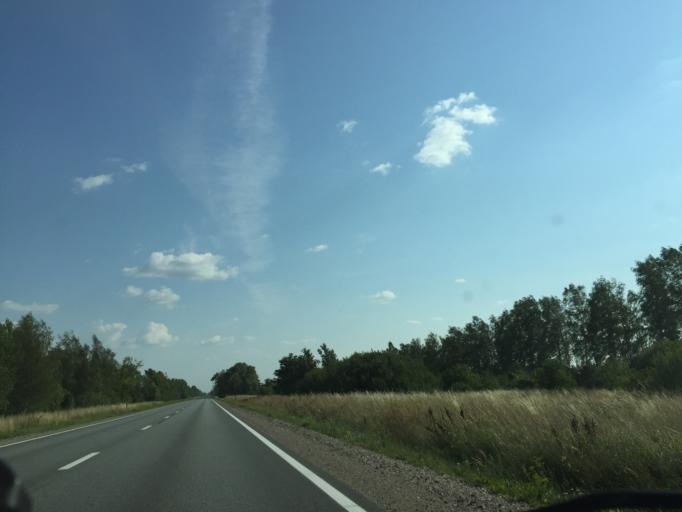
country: LV
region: Jelgava
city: Jelgava
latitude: 56.4609
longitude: 23.6922
